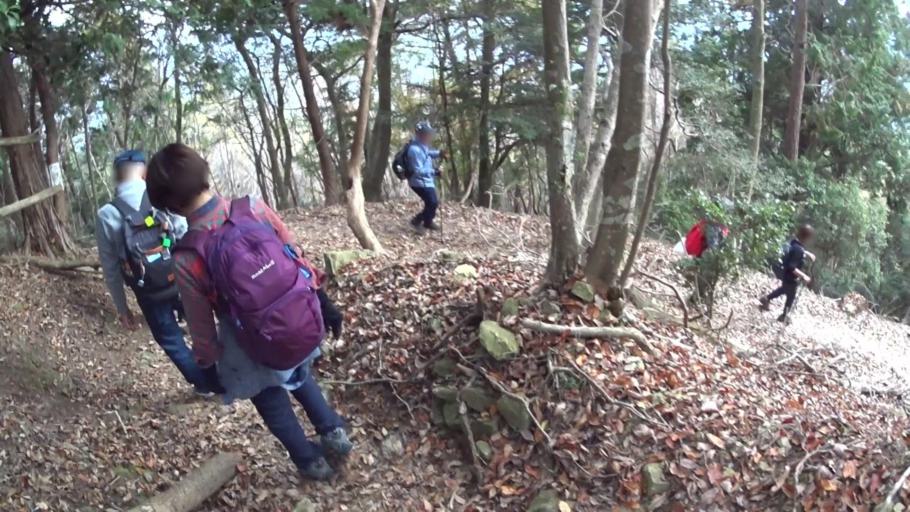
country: JP
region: Kyoto
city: Kameoka
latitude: 35.0574
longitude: 135.6437
